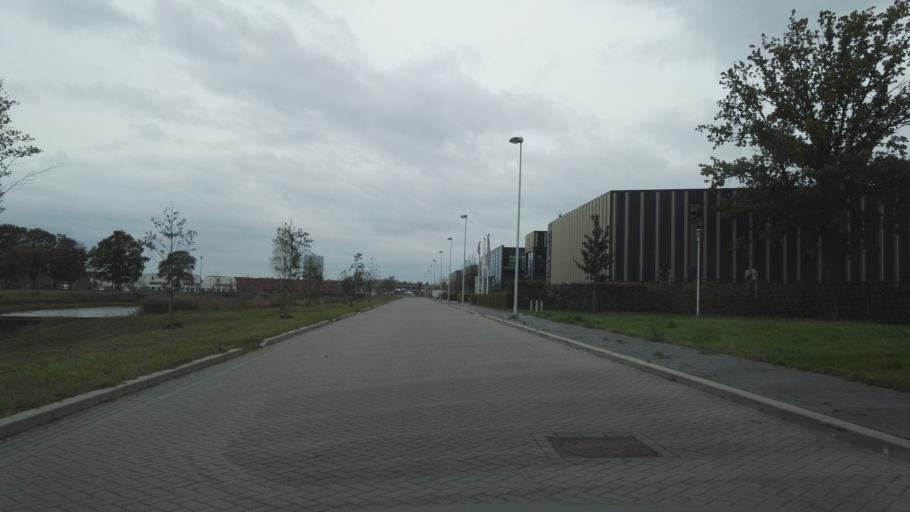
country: NL
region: Gelderland
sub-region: Gemeente Apeldoorn
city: Apeldoorn
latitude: 52.2444
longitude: 6.0009
